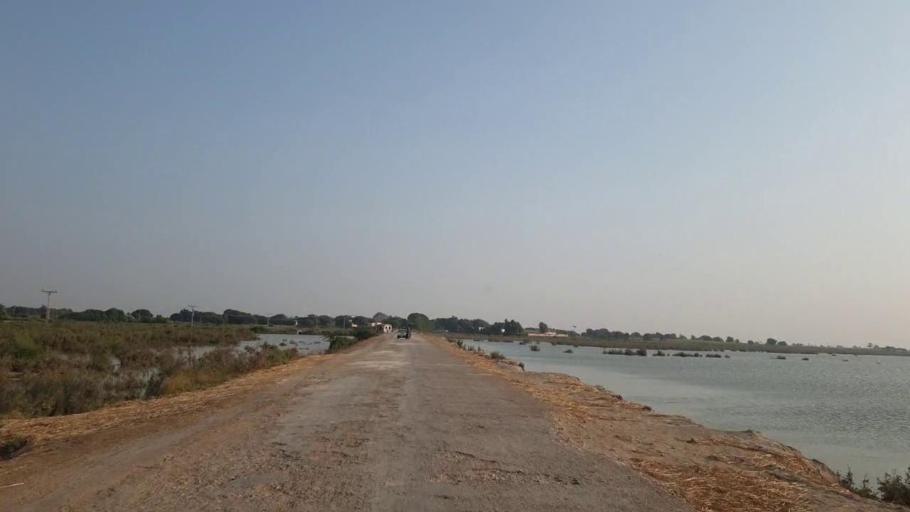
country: PK
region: Sindh
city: Bulri
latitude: 24.9900
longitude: 68.3882
